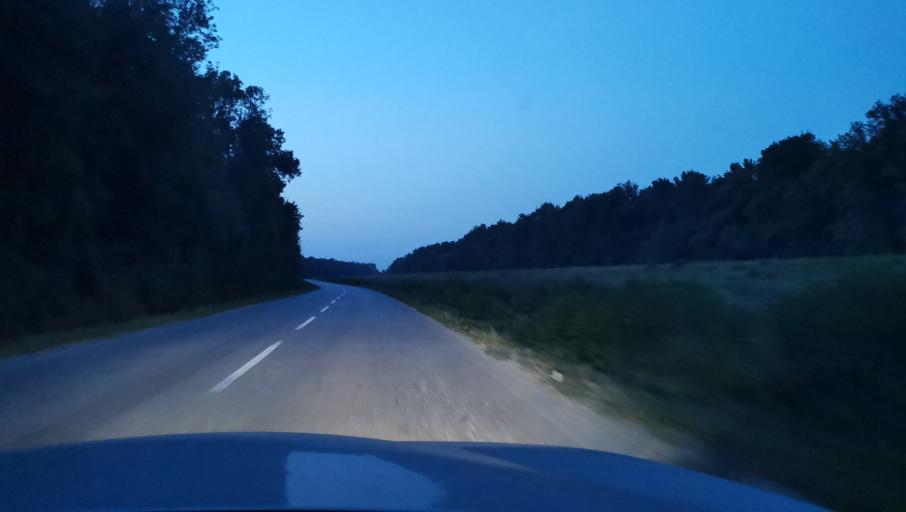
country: RS
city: Boljevci
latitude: 44.7002
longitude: 20.2020
